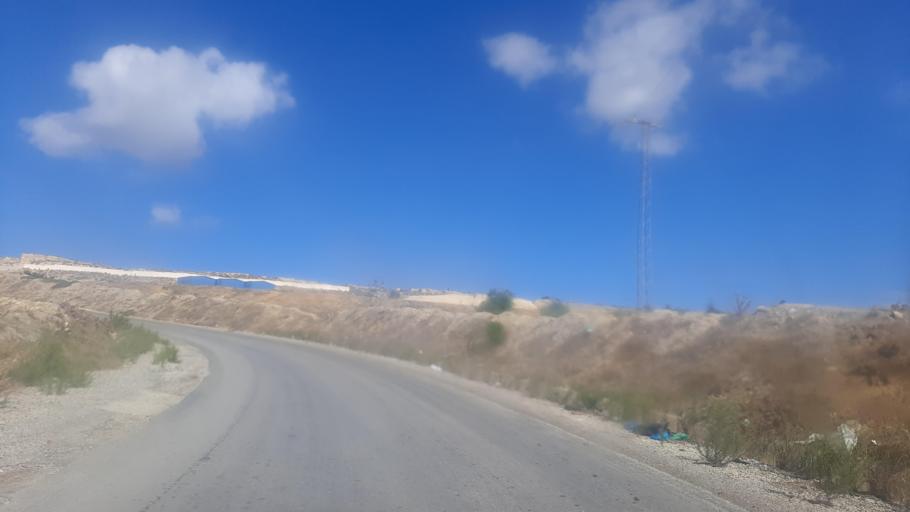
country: TN
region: Nabul
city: Nabeul
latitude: 36.4916
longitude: 10.7060
